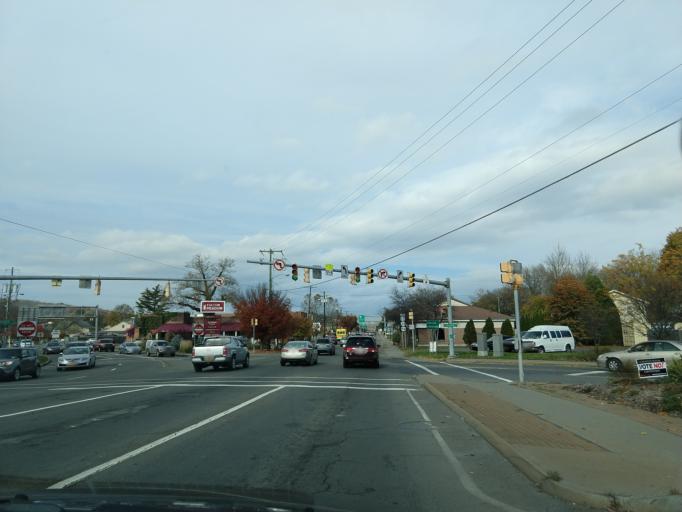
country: US
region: New York
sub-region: Tompkins County
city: Ithaca
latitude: 42.4364
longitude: -76.5082
